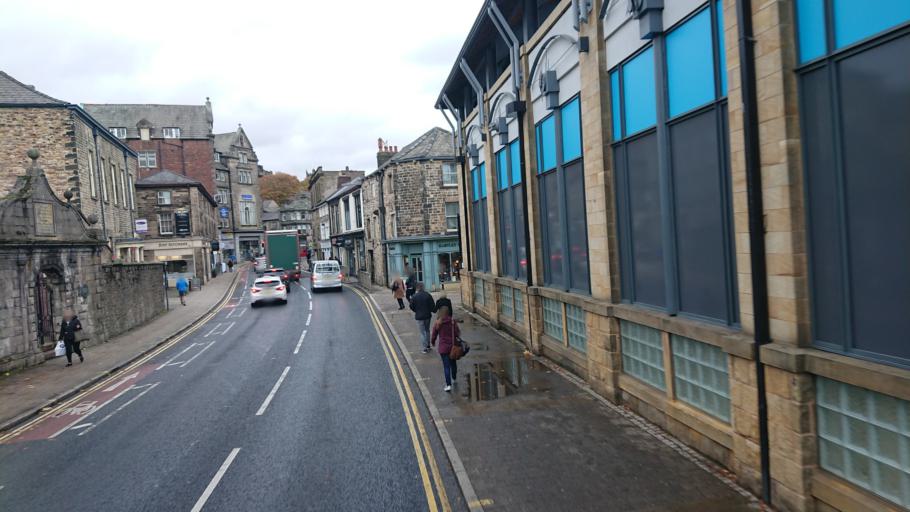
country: GB
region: England
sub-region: Lancashire
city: Lancaster
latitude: 54.0478
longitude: -2.8021
